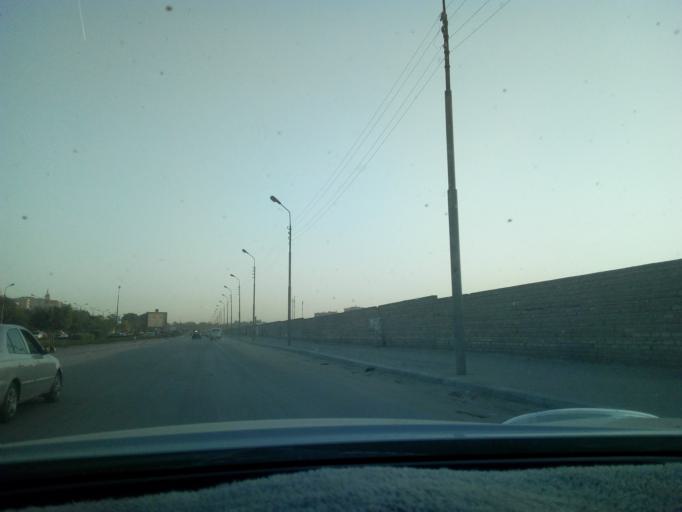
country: EG
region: Muhafazat al Qalyubiyah
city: Al Khankah
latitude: 30.1251
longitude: 31.3629
